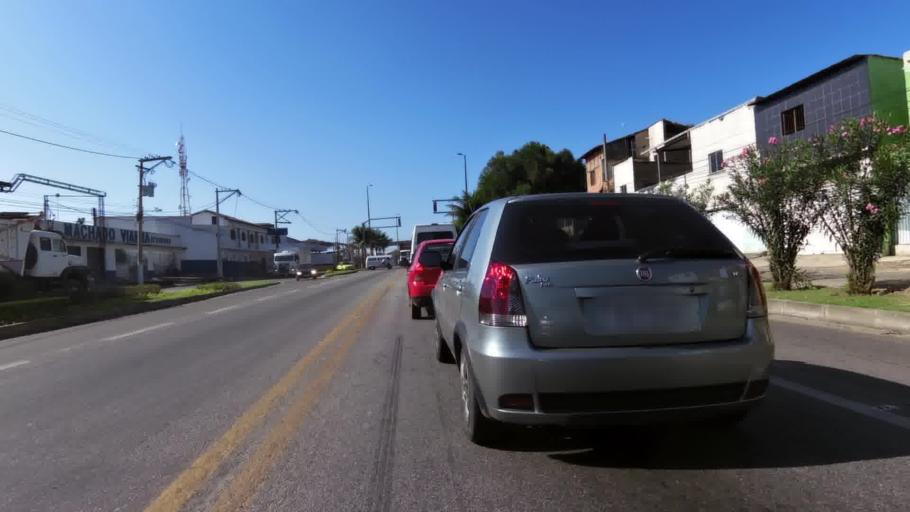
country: BR
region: Rio de Janeiro
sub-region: Campos Dos Goytacazes
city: Campos
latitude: -21.7285
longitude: -41.3225
